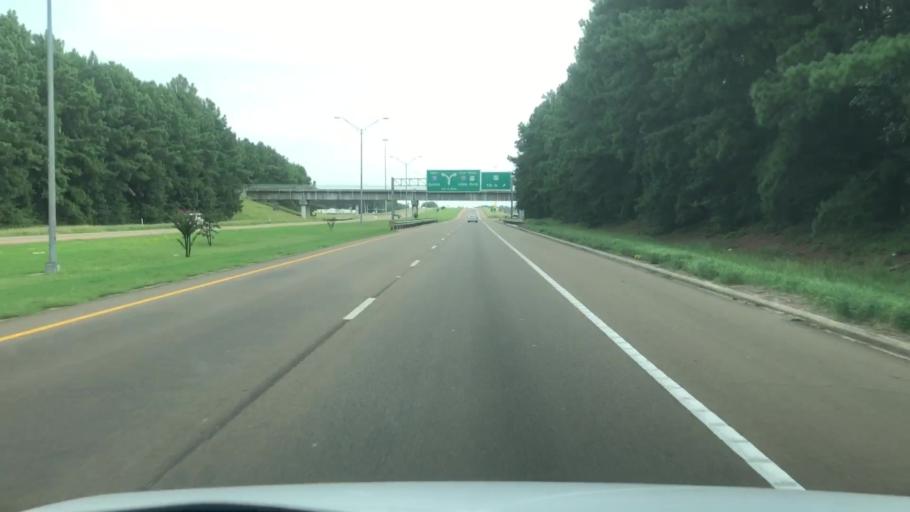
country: US
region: Texas
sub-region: Bowie County
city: Wake Village
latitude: 33.4129
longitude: -94.0970
